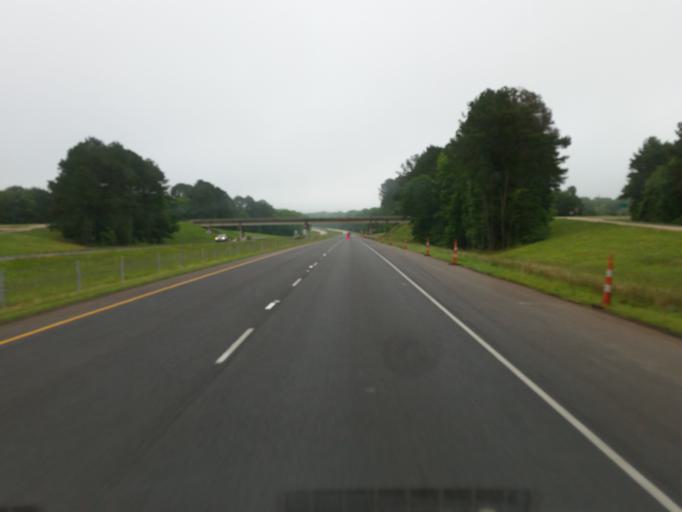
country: US
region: Louisiana
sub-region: Webster Parish
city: Minden
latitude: 32.5634
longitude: -93.1620
